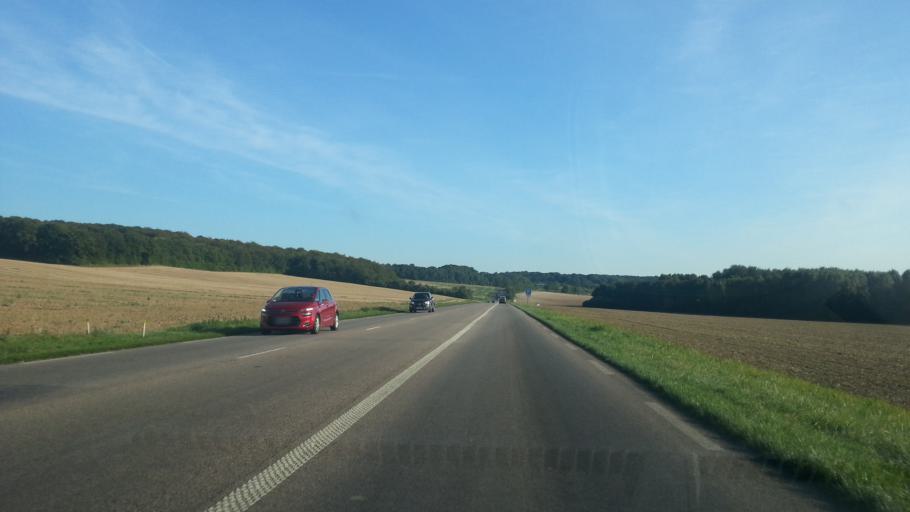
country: FR
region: Picardie
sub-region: Departement de l'Oise
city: Troissereux
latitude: 49.4697
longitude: 2.0569
